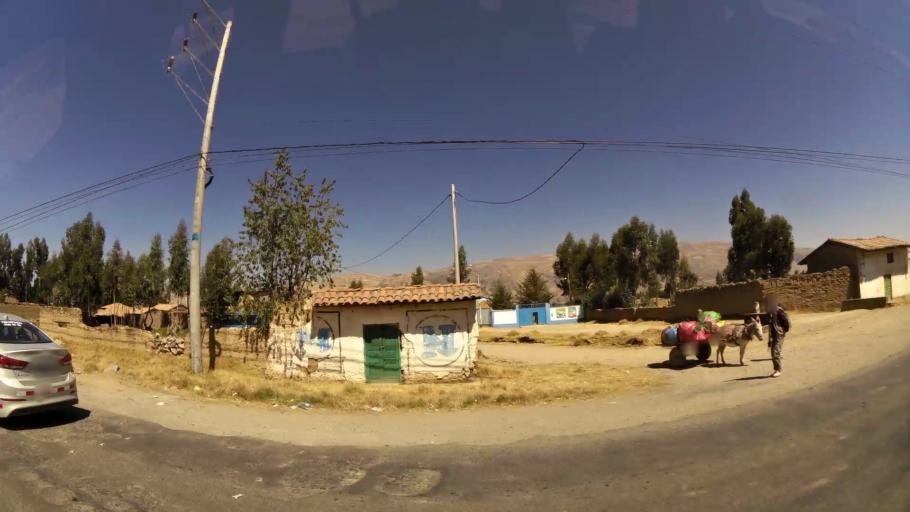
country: PE
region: Junin
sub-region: Provincia de Jauja
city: San Lorenzo
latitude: -11.8498
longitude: -75.3833
